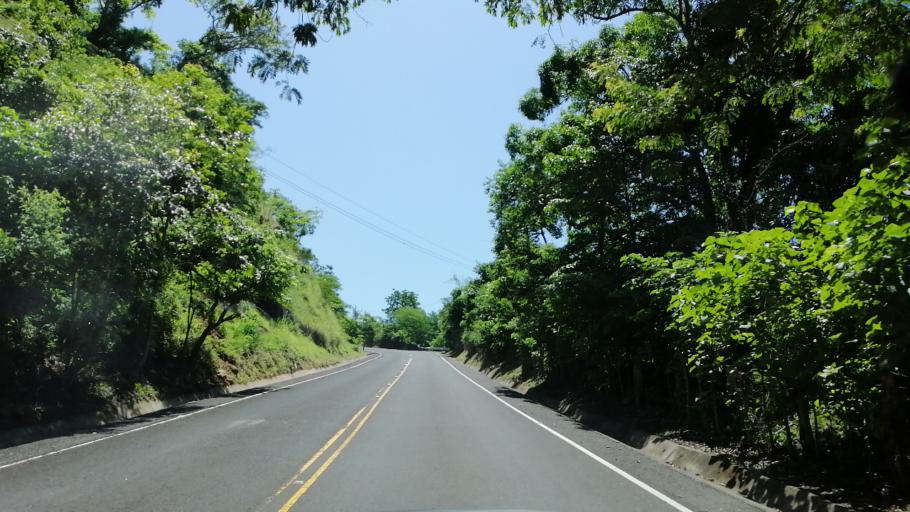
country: SV
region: San Miguel
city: Sesori
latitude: 13.8049
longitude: -88.3946
